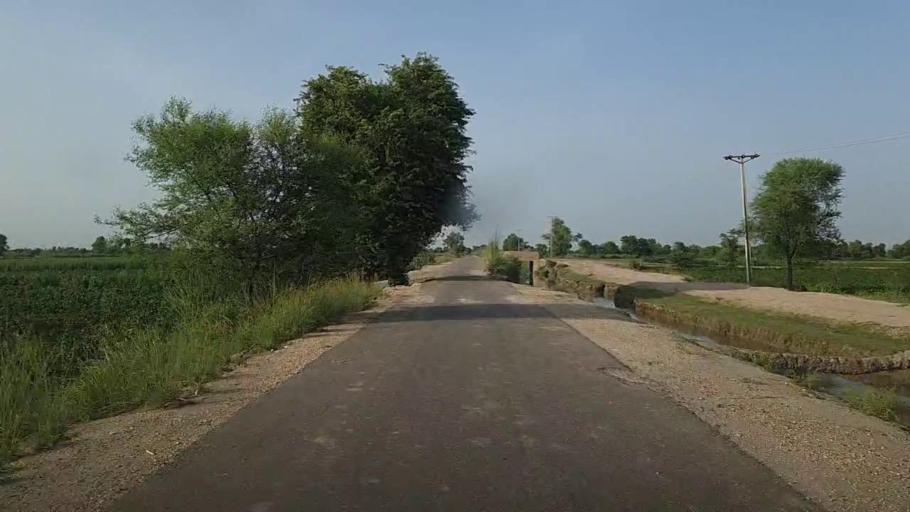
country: PK
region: Sindh
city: Ubauro
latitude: 28.0887
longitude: 69.8183
